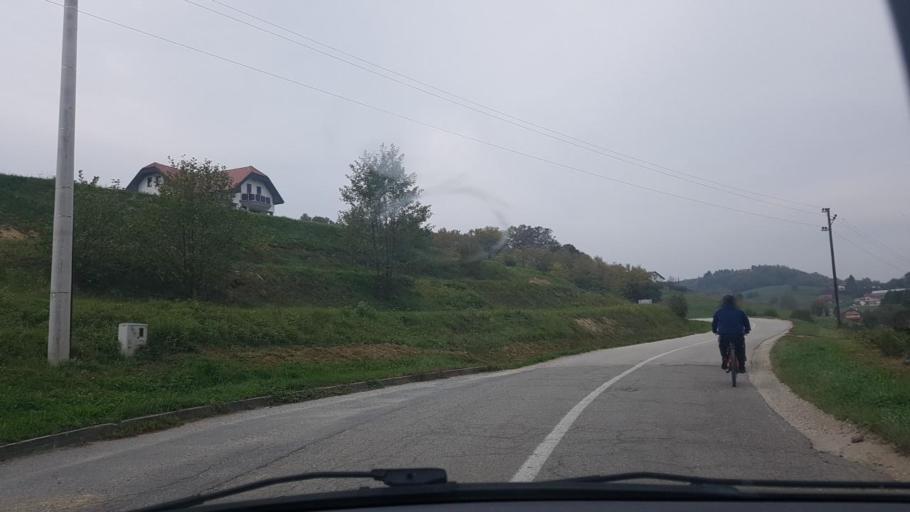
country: SI
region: Rogatec
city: Rogatec
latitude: 46.1938
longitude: 15.6956
